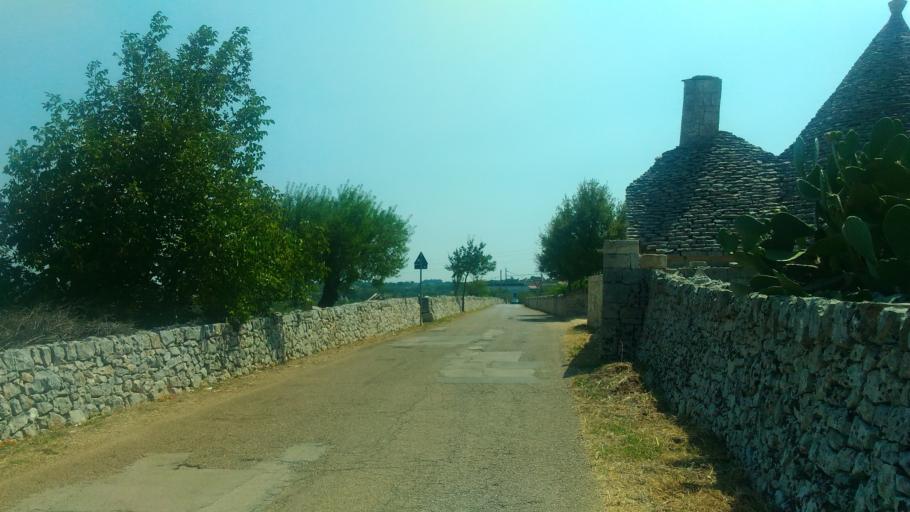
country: IT
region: Apulia
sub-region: Provincia di Brindisi
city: Cisternino
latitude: 40.7452
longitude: 17.3786
